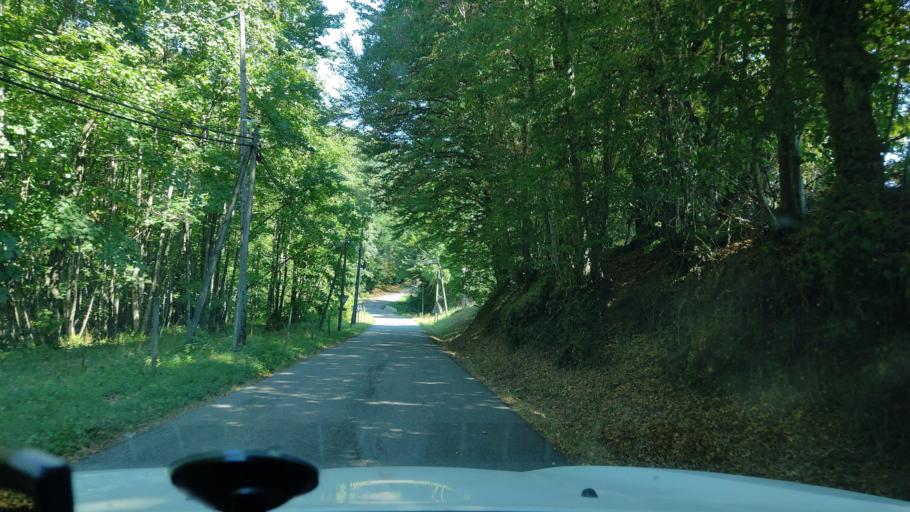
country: FR
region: Rhone-Alpes
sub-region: Departement de la Savoie
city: Le Bourget-du-Lac
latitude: 45.6295
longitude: 5.8496
